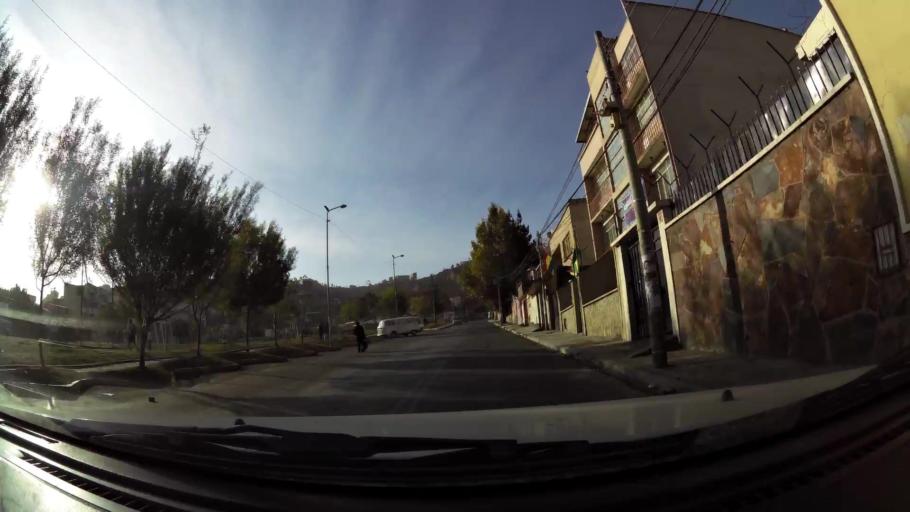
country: BO
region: La Paz
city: La Paz
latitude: -16.5211
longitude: -68.1042
